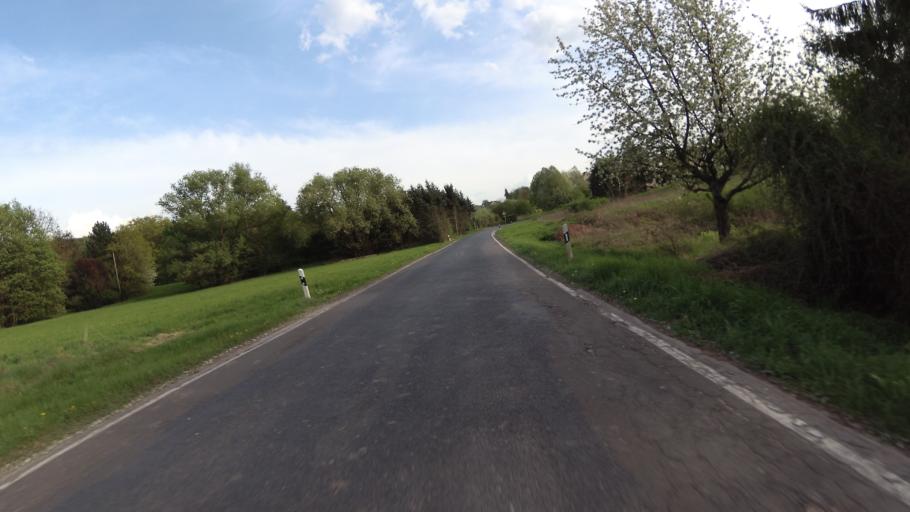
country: DE
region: Rheinland-Pfalz
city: Urzig
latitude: 49.9870
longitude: 7.0018
